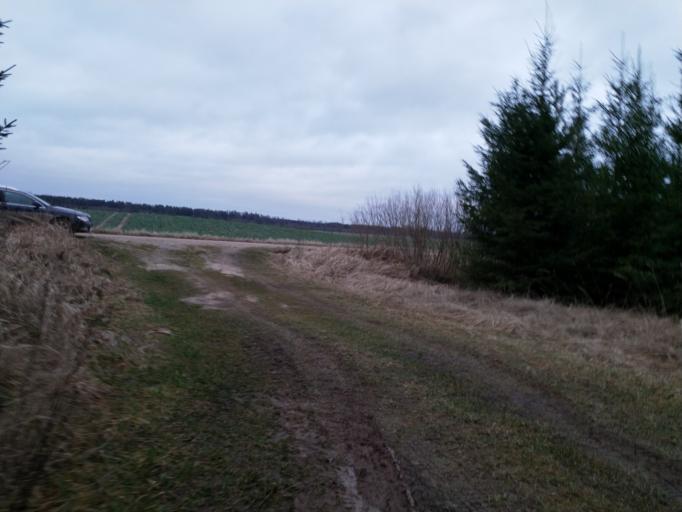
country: LV
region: Saldus Rajons
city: Saldus
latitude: 56.8946
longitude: 22.3306
